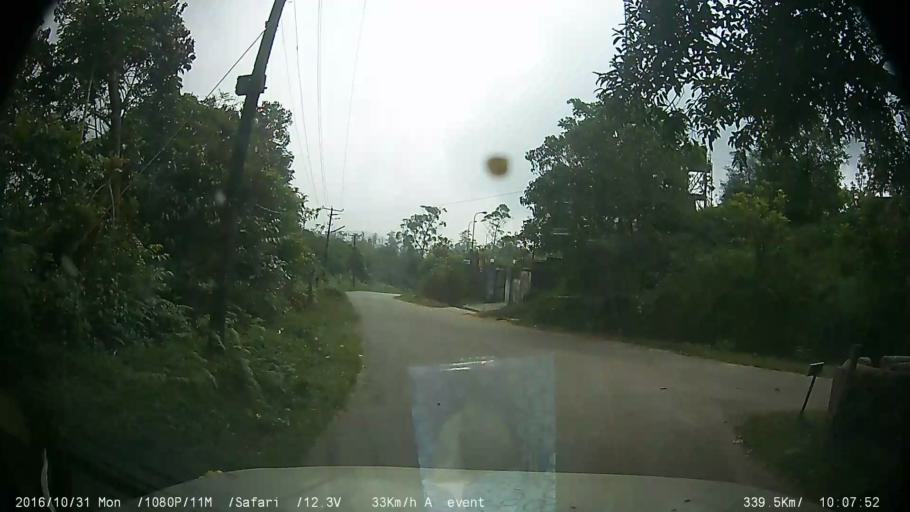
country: IN
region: Karnataka
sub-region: Kodagu
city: Madikeri
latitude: 12.4165
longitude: 75.7347
